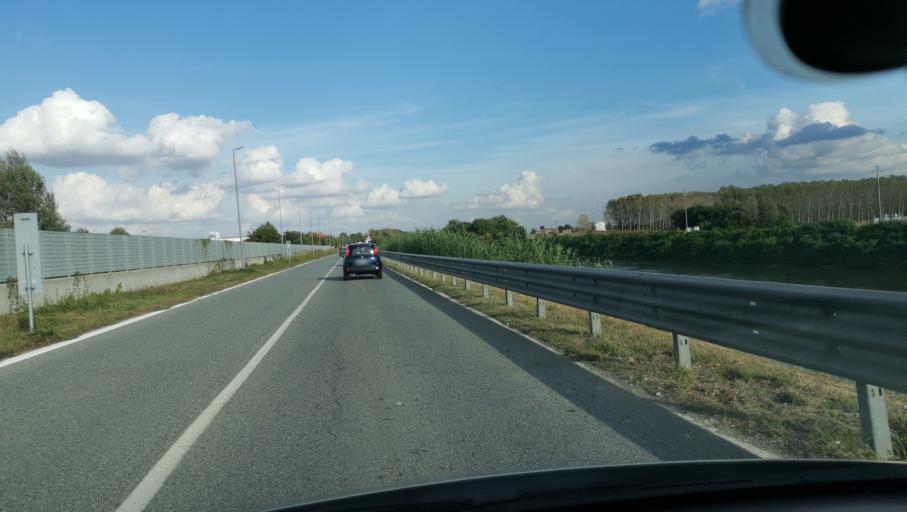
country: IT
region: Piedmont
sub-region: Provincia di Torino
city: Chivasso
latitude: 45.1918
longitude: 7.9096
